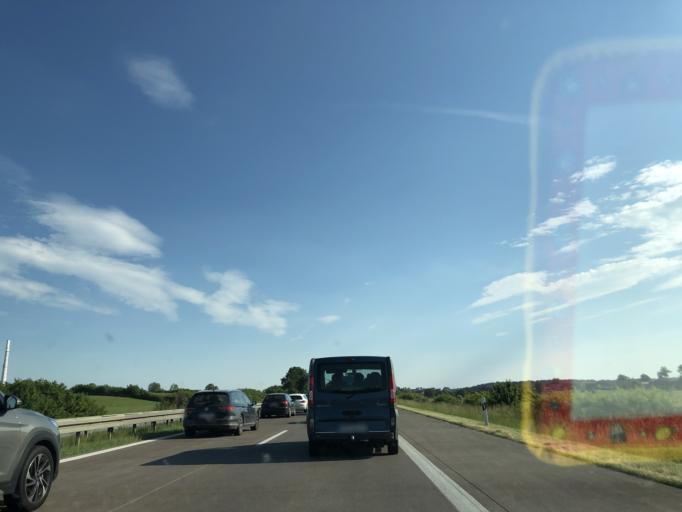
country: DE
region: Brandenburg
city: Althuttendorf
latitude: 52.9693
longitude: 13.8149
